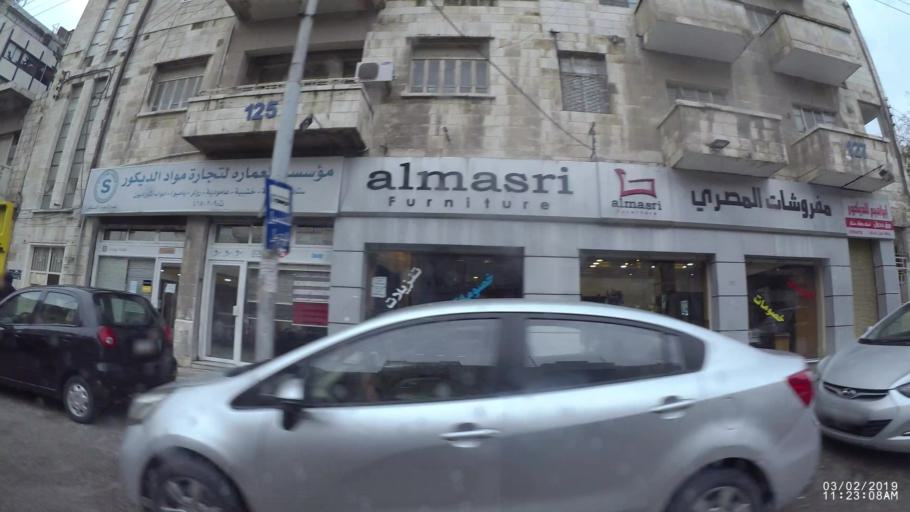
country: JO
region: Amman
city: Amman
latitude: 31.9527
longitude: 35.9246
